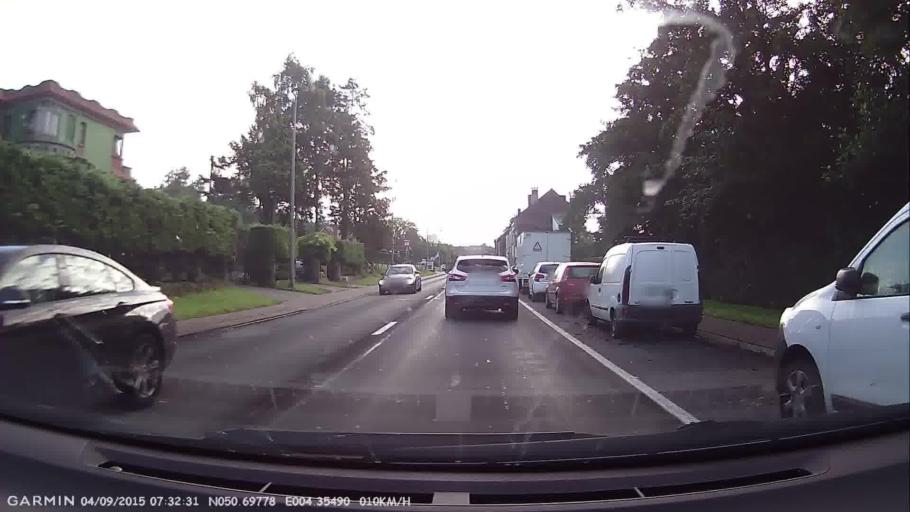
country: BE
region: Wallonia
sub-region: Province du Brabant Wallon
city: Braine-l'Alleud
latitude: 50.6978
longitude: 4.3550
